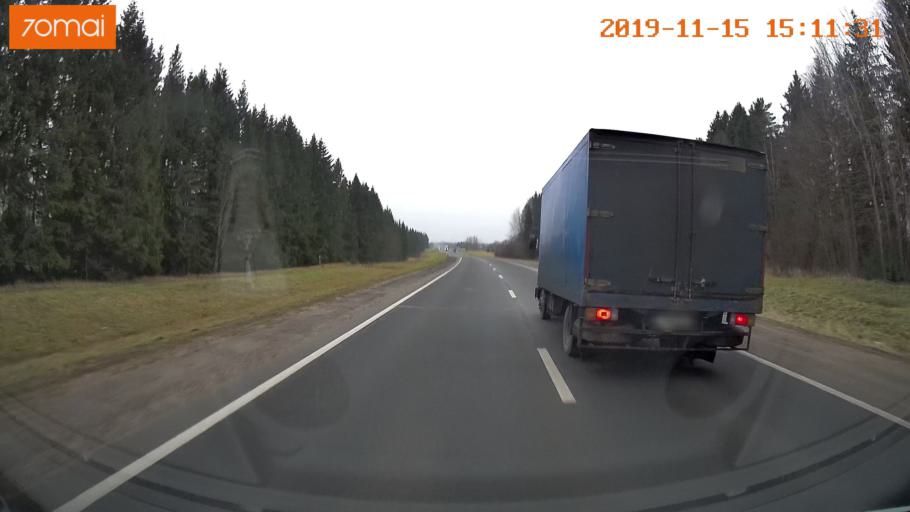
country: RU
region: Jaroslavl
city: Prechistoye
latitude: 58.3356
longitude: 40.2399
